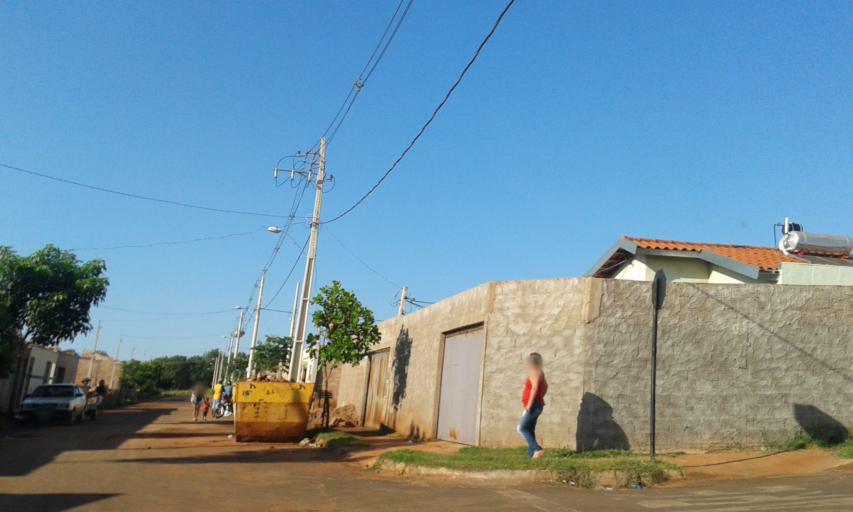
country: BR
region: Minas Gerais
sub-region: Ituiutaba
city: Ituiutaba
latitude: -19.0152
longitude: -49.4528
